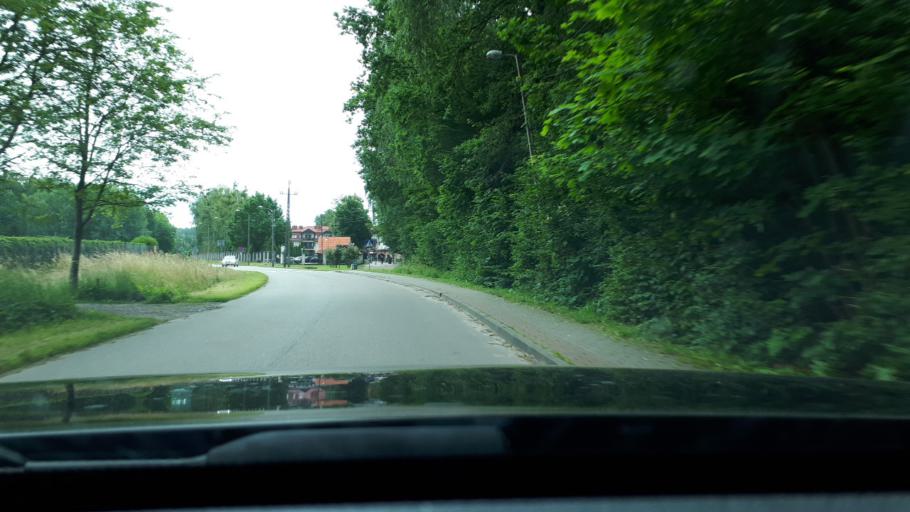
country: PL
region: Warmian-Masurian Voivodeship
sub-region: Powiat ostrodzki
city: Ostroda
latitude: 53.6900
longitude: 20.0957
